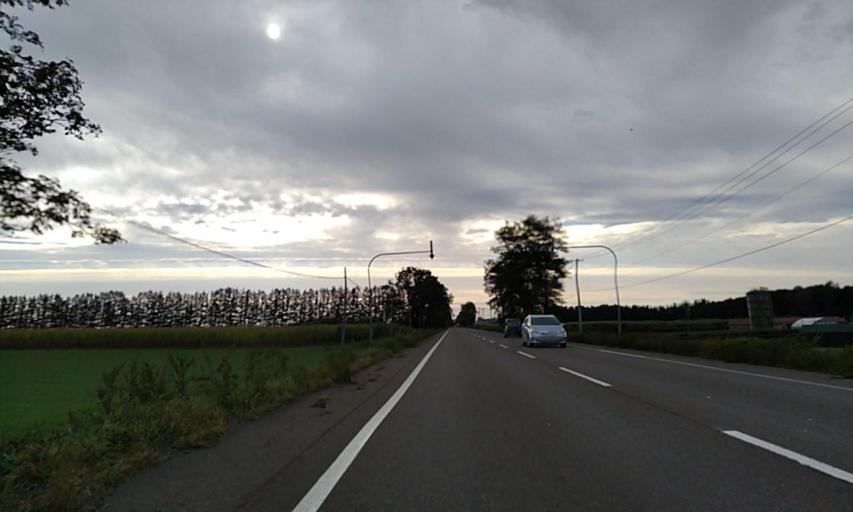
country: JP
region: Hokkaido
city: Obihiro
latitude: 42.9257
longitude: 142.9873
